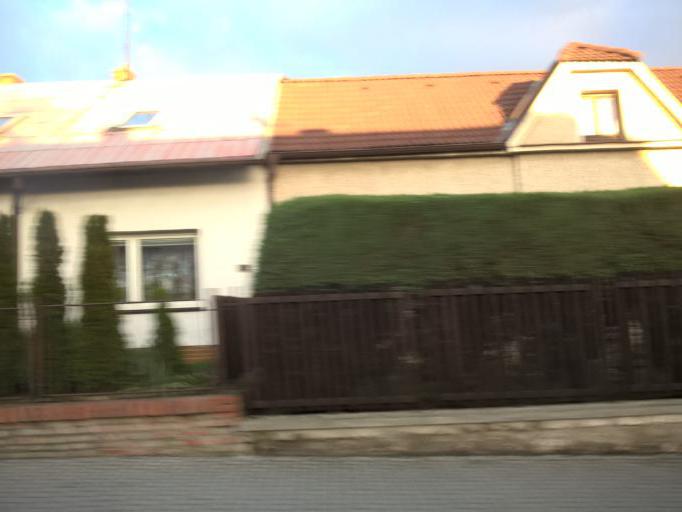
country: CZ
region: Central Bohemia
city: Horomerice
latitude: 50.0914
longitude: 14.3245
